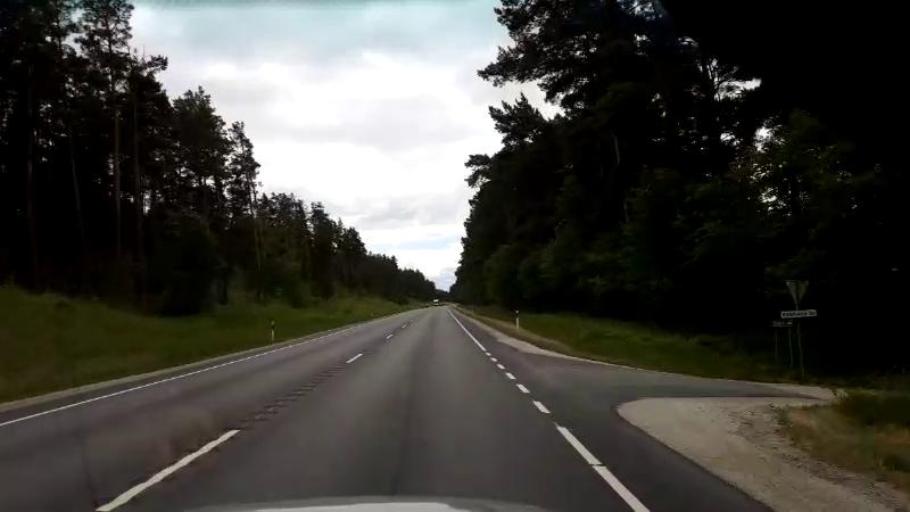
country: EE
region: Paernumaa
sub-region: Paernu linn
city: Parnu
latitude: 58.1694
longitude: 24.4957
